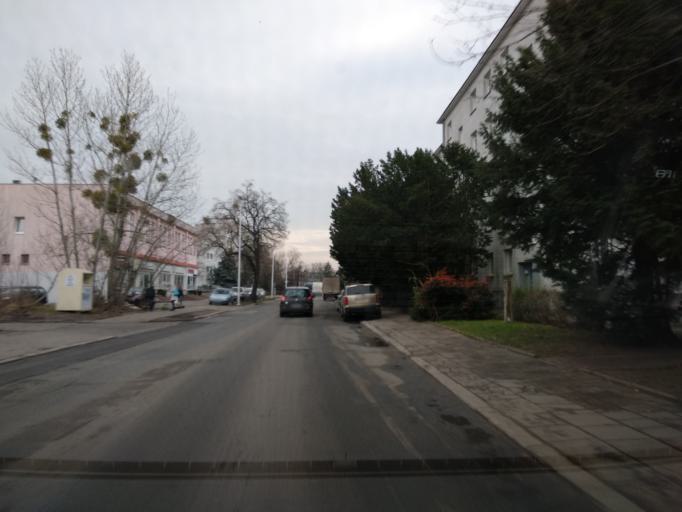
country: PL
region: Lower Silesian Voivodeship
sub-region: Powiat wroclawski
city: Wroclaw
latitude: 51.0947
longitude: 16.9911
